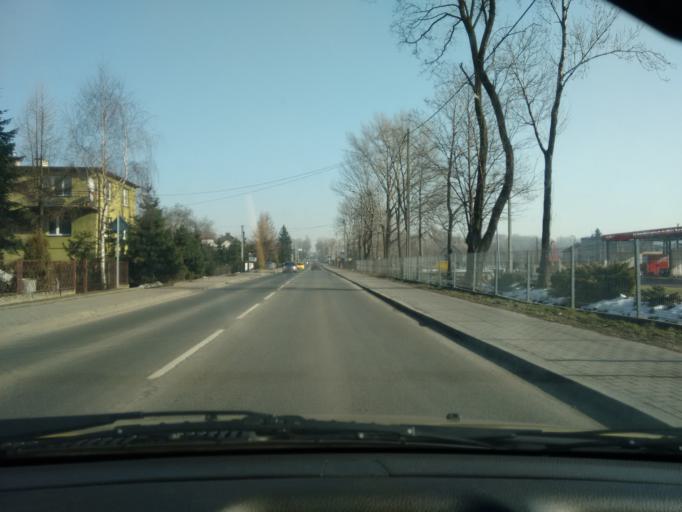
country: PL
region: Lesser Poland Voivodeship
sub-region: Powiat oswiecimski
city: Kety
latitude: 49.8834
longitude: 19.2326
